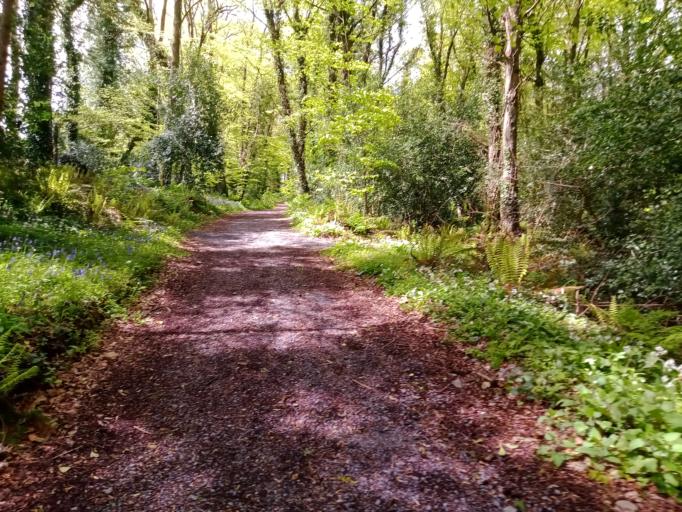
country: IE
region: Leinster
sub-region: Kilkenny
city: Thomastown
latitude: 52.4811
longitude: -7.0568
